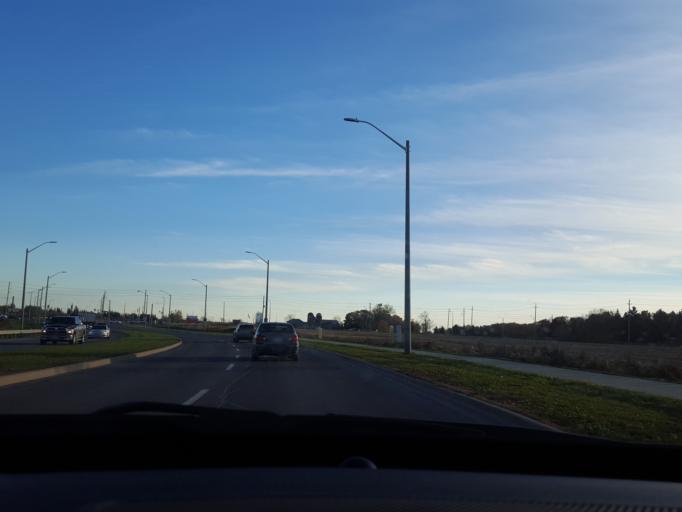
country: CA
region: Ontario
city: Markham
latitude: 43.8851
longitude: -79.2154
